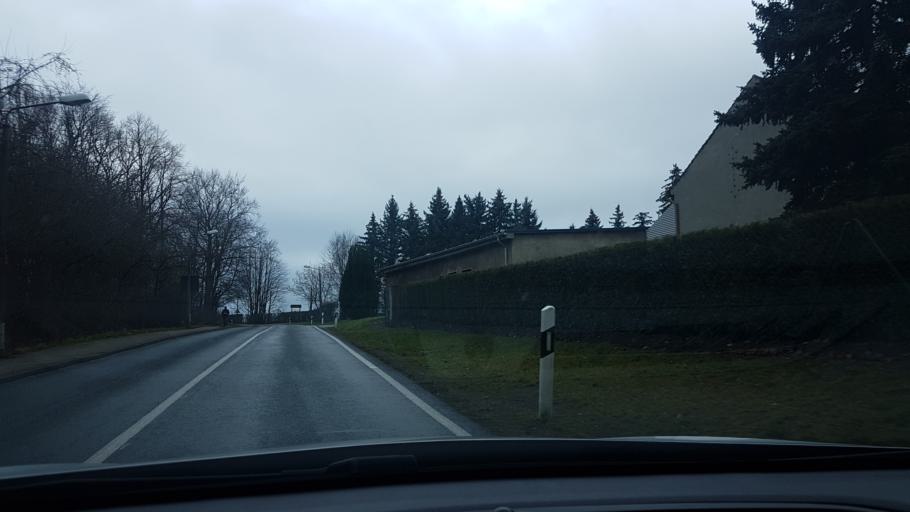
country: DE
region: Saxony
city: Goerlitz
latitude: 51.1326
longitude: 14.9586
